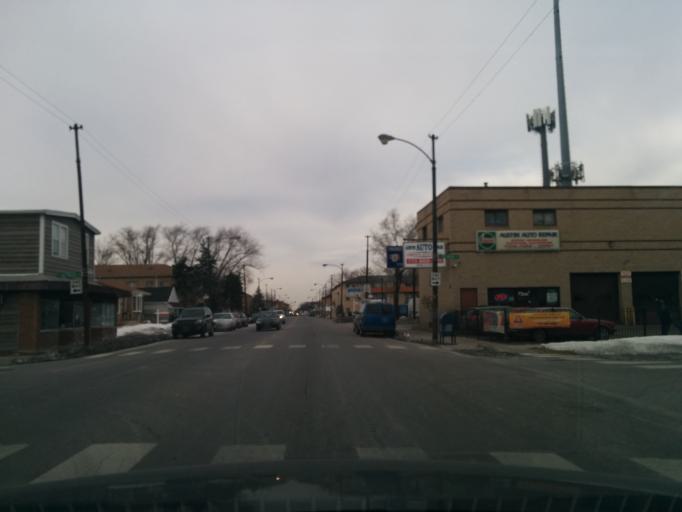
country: US
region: Illinois
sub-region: Cook County
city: Elmwood Park
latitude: 41.9381
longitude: -87.8089
